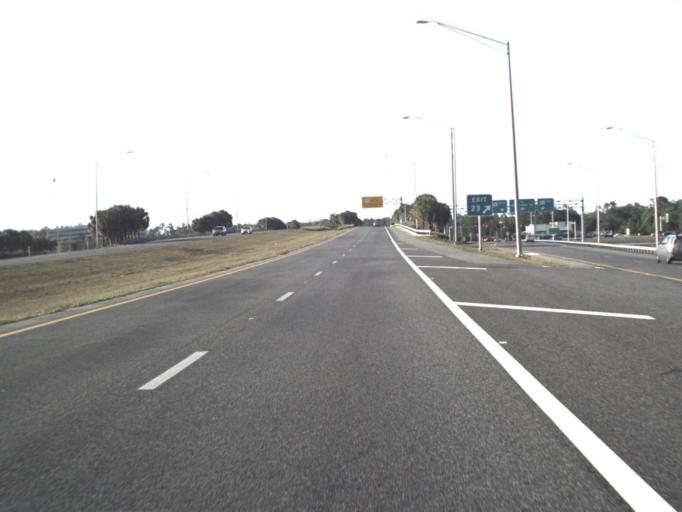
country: US
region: Florida
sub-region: Orange County
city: Alafaya
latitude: 28.5613
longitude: -81.1910
